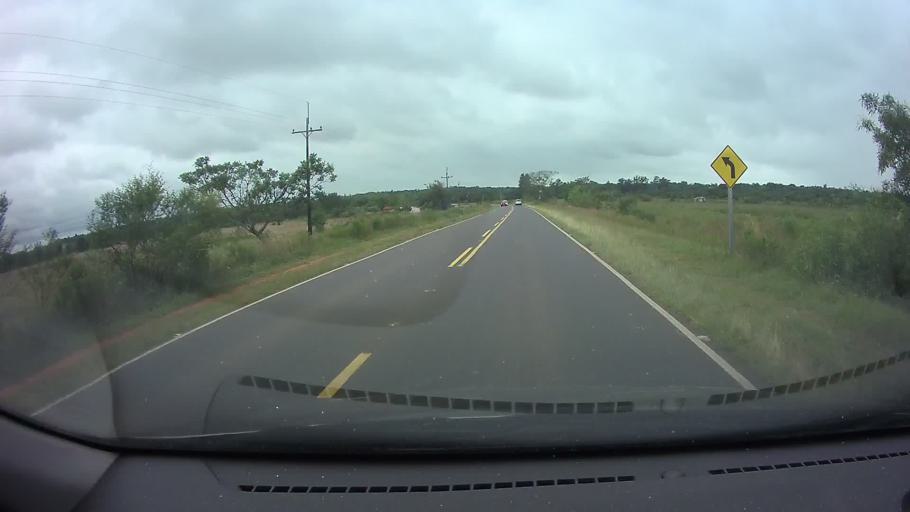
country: PY
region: Central
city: Nueva Italia
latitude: -25.6119
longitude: -57.4505
